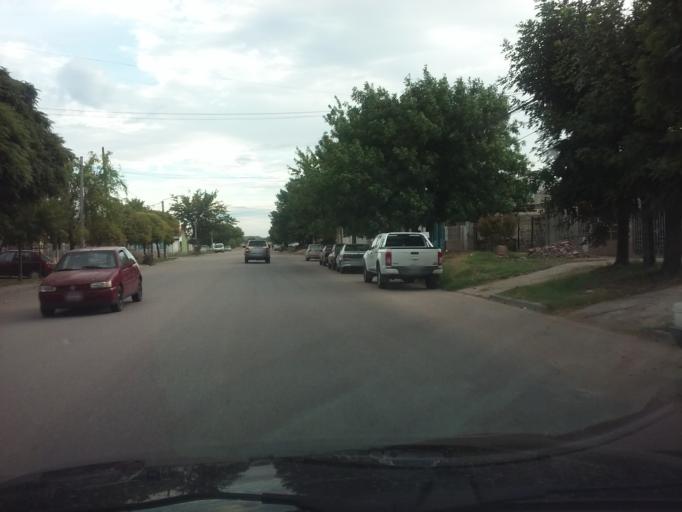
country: AR
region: La Pampa
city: Santa Rosa
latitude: -36.6443
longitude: -64.2950
